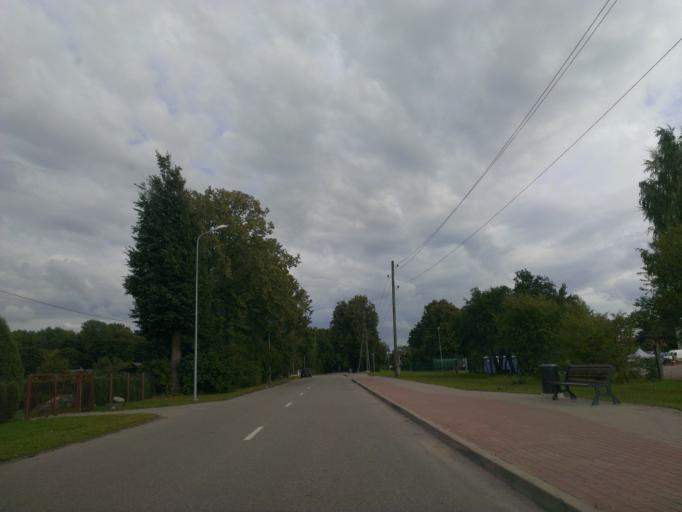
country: LV
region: Ikskile
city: Ikskile
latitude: 56.8314
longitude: 24.4854
